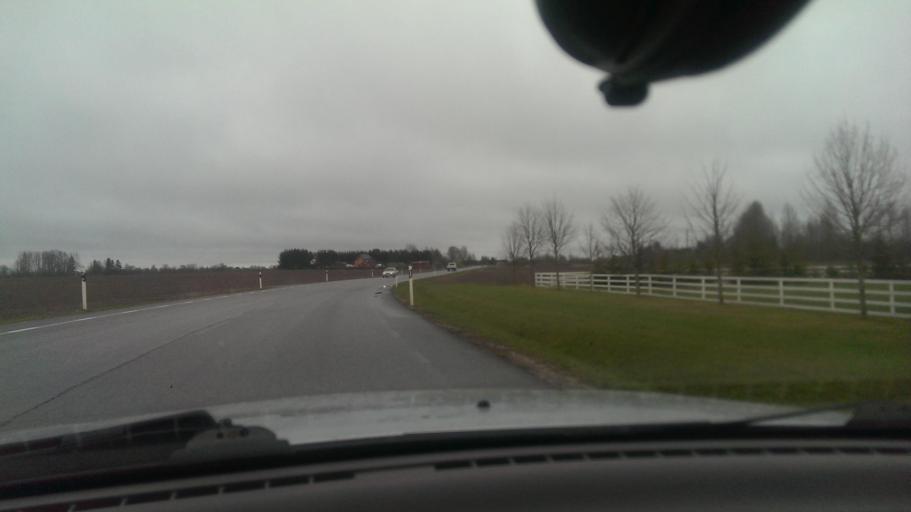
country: EE
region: Tartu
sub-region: Tartu linn
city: Tartu
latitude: 58.3861
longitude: 26.7876
